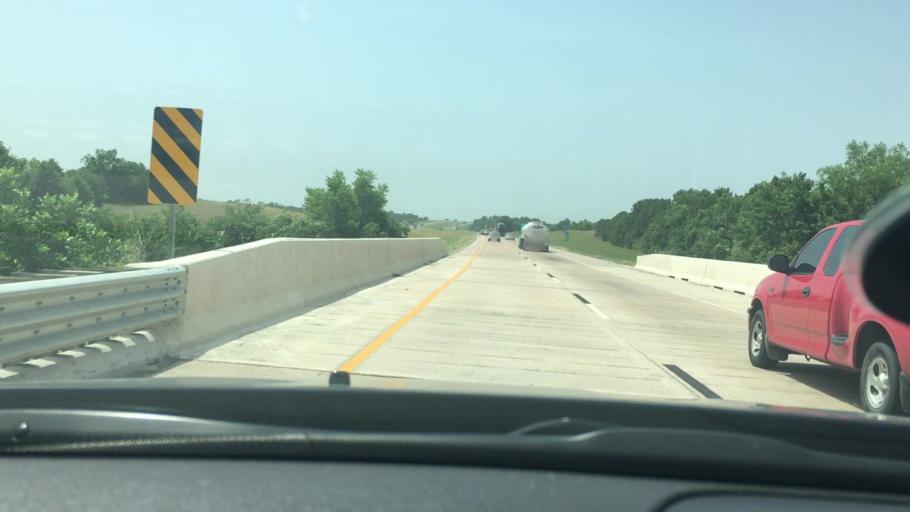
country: US
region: Oklahoma
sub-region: Garvin County
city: Wynnewood
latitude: 34.6458
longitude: -97.2200
